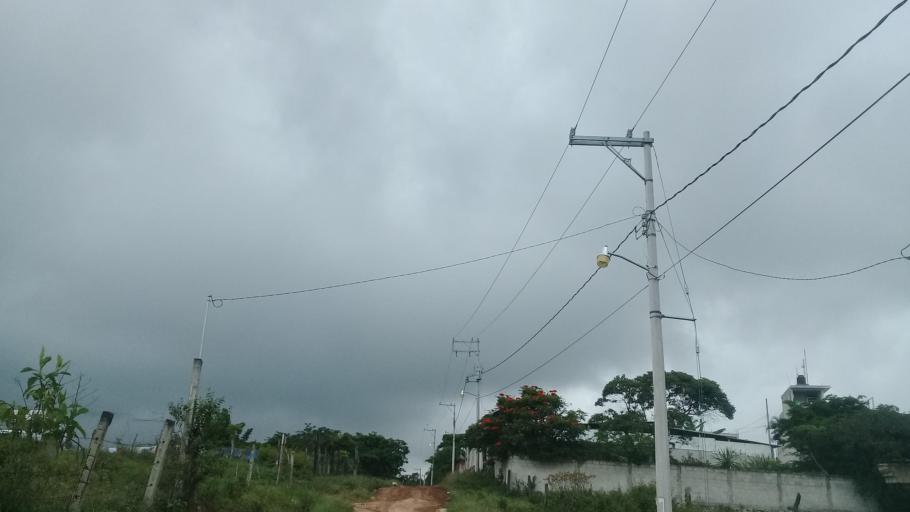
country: MX
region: Veracruz
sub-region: Emiliano Zapata
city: Jacarandas
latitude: 19.4923
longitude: -96.8543
